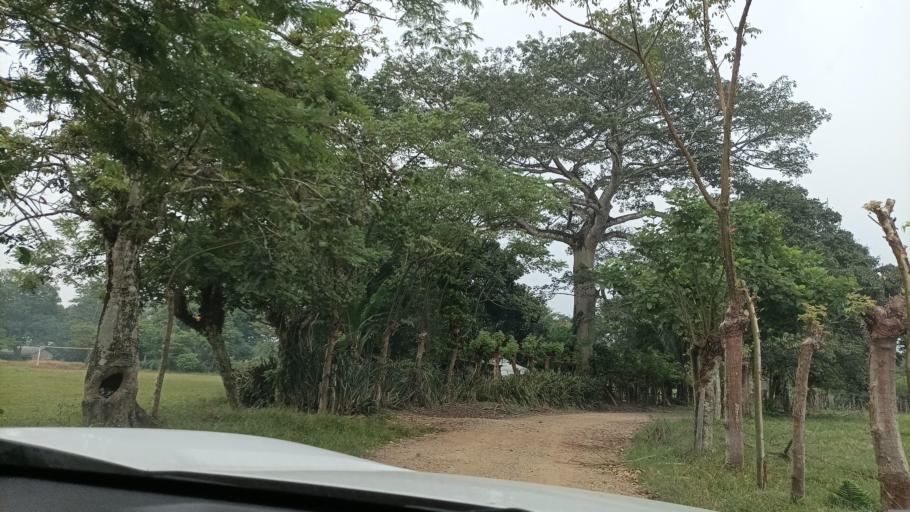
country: MX
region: Veracruz
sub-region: Uxpanapa
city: Poblado 10
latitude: 17.5425
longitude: -94.2365
